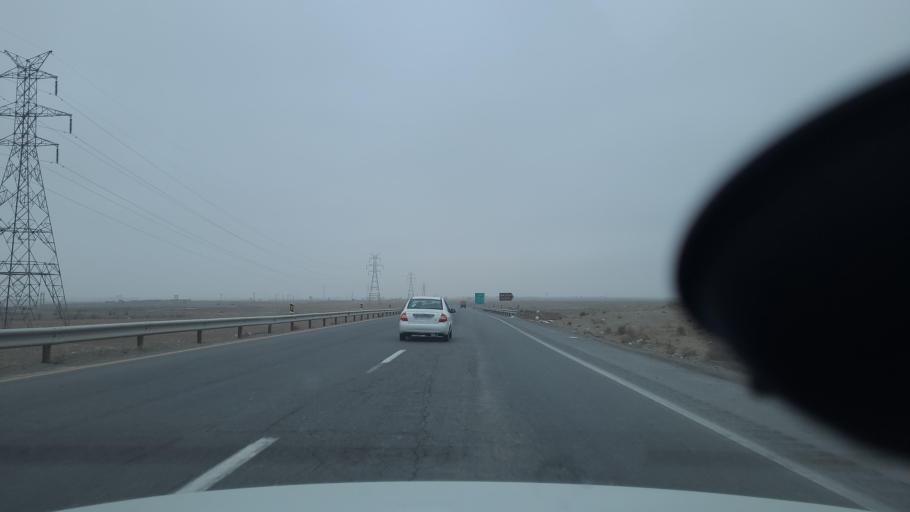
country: IR
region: Razavi Khorasan
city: Fariman
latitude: 35.9726
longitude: 59.7471
